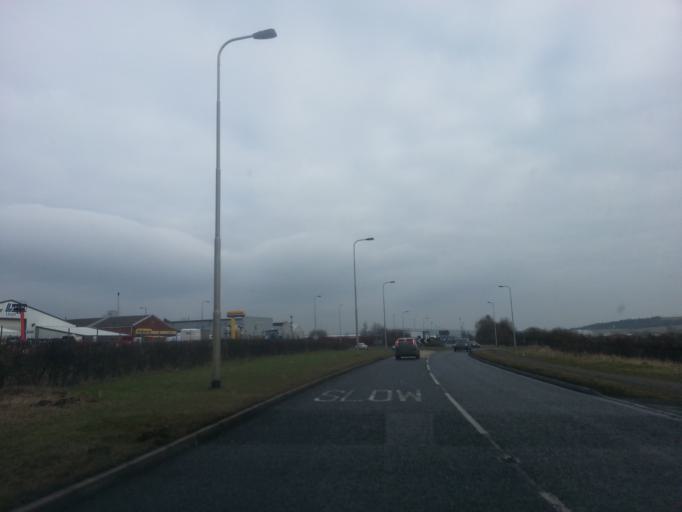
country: GB
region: England
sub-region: County Durham
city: Bishop Auckland
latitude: 54.6356
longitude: -1.6993
